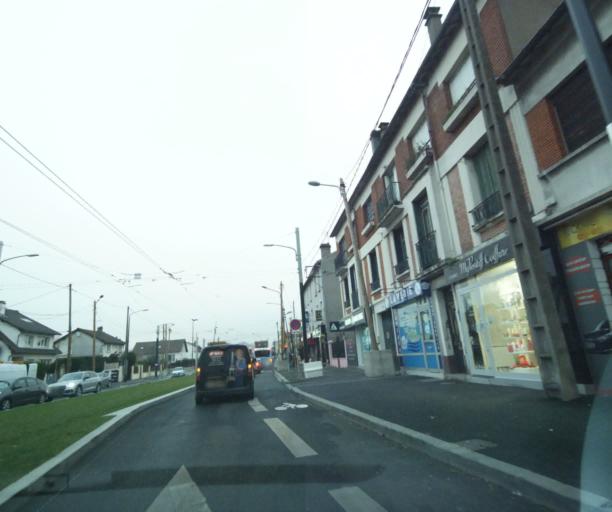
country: FR
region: Ile-de-France
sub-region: Departement de Seine-Saint-Denis
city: Le Raincy
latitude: 48.9096
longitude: 2.5269
